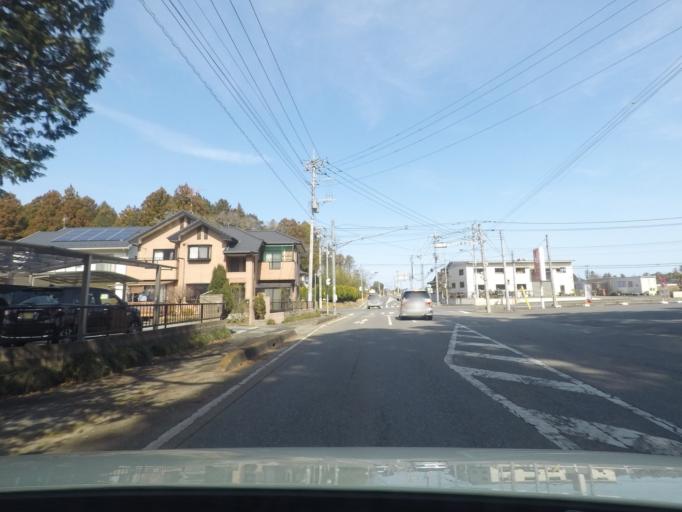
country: JP
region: Ibaraki
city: Okunoya
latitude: 36.2103
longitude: 140.4443
